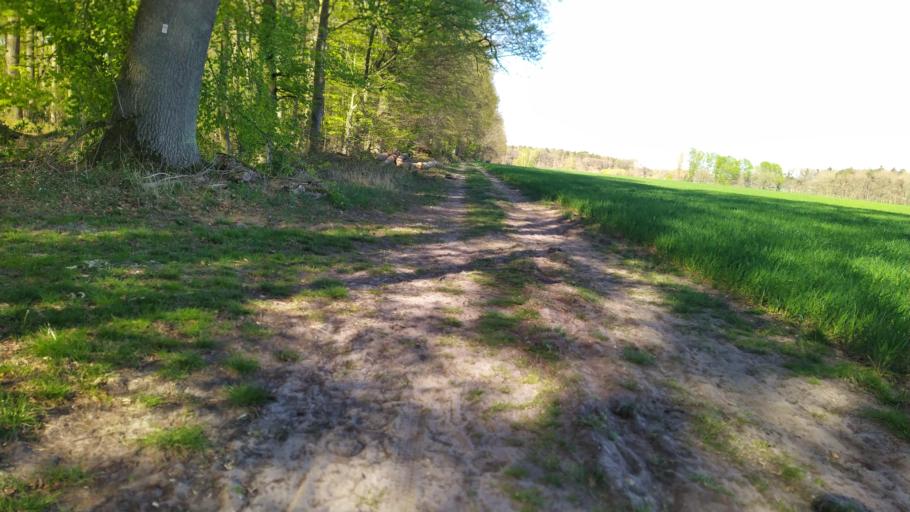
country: DE
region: Lower Saxony
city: Klein Meckelsen
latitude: 53.2962
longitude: 9.4290
